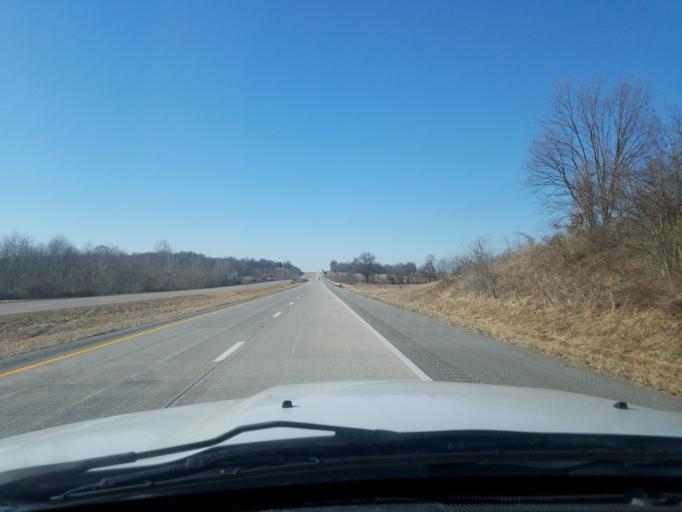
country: US
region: Kentucky
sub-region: Henderson County
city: Henderson
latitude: 37.7799
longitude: -87.4529
